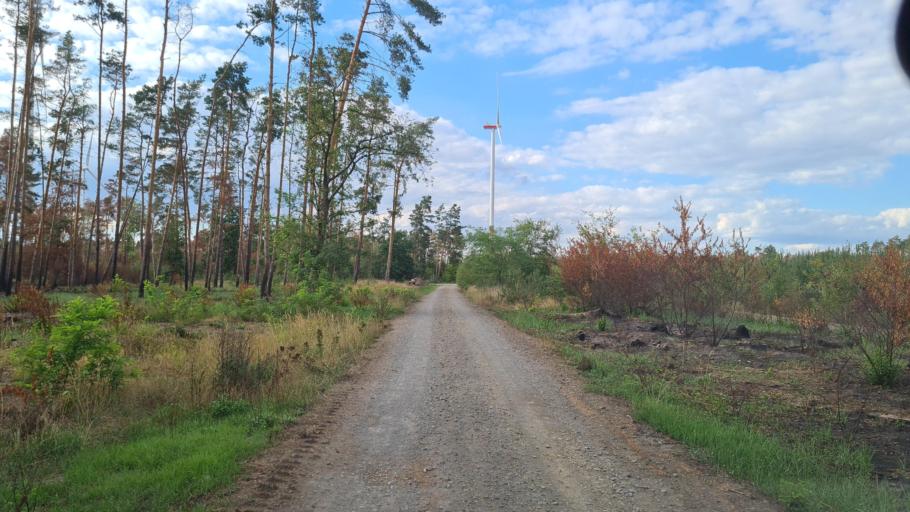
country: DE
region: Saxony
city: Arzberg
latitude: 51.5639
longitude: 13.1821
